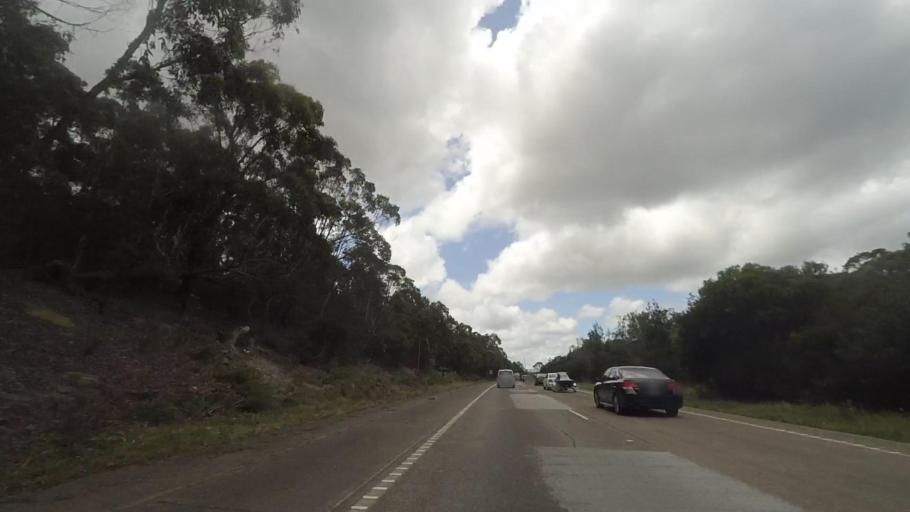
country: AU
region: New South Wales
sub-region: Gosford Shire
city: Narara
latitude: -33.3990
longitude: 151.2969
